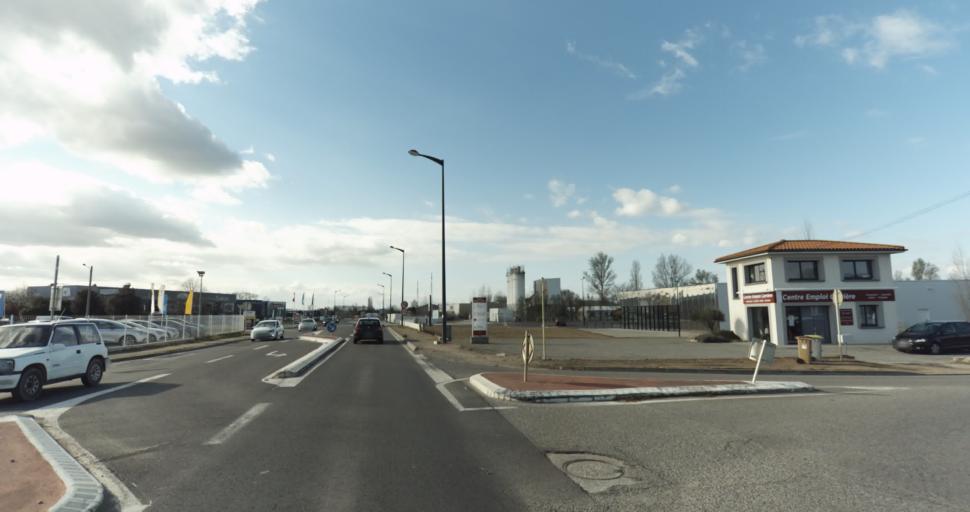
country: FR
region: Midi-Pyrenees
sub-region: Departement de la Haute-Garonne
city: Auterive
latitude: 43.3611
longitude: 1.4632
